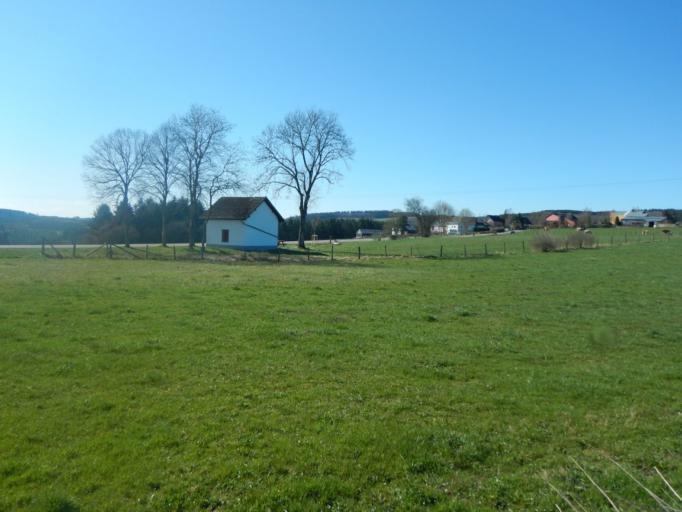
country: LU
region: Diekirch
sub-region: Canton de Wiltz
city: Eschweiler
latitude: 49.9932
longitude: 5.9531
